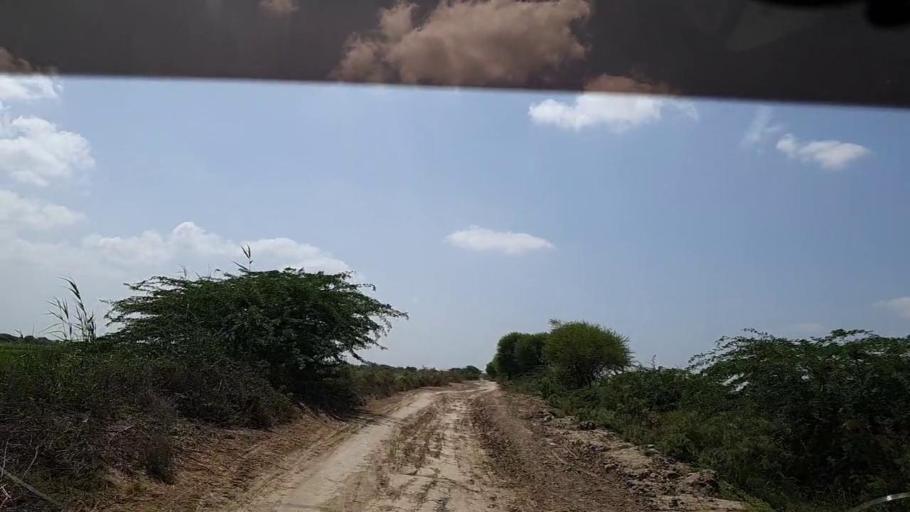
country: PK
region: Sindh
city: Badin
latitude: 24.5579
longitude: 68.7413
